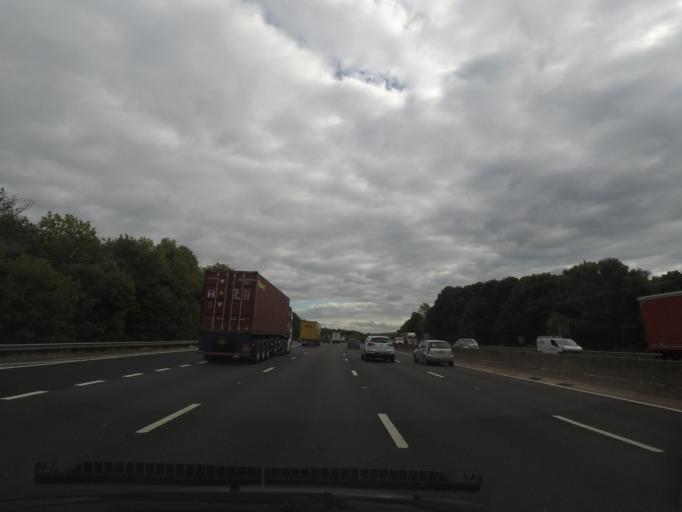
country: GB
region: England
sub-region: Sheffield
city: Chapletown
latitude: 53.4607
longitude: -1.4472
